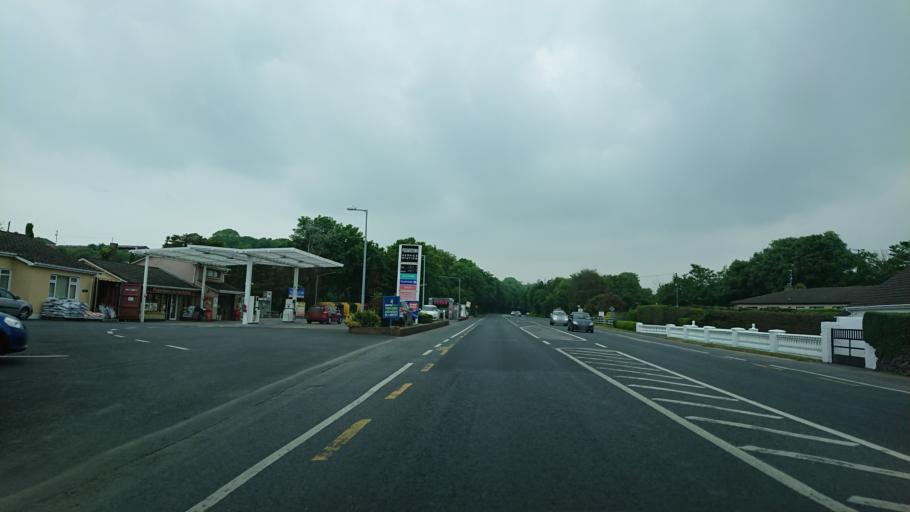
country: IE
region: Munster
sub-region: Waterford
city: Tra Mhor
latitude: 52.1752
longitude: -7.1379
